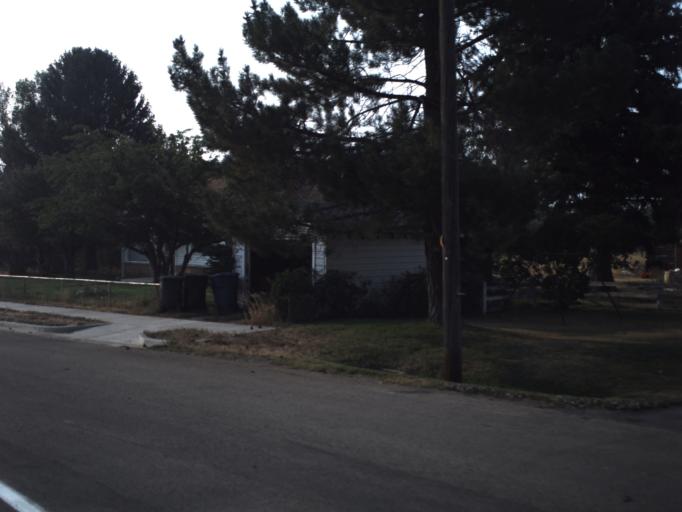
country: US
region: Utah
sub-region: Summit County
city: Kamas
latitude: 40.6432
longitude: -111.2736
